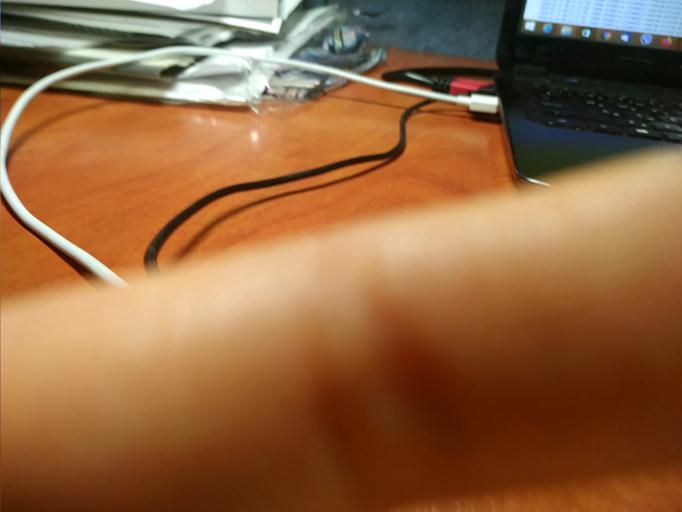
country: RU
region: Tverskaya
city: Rameshki
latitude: 57.3317
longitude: 35.9500
